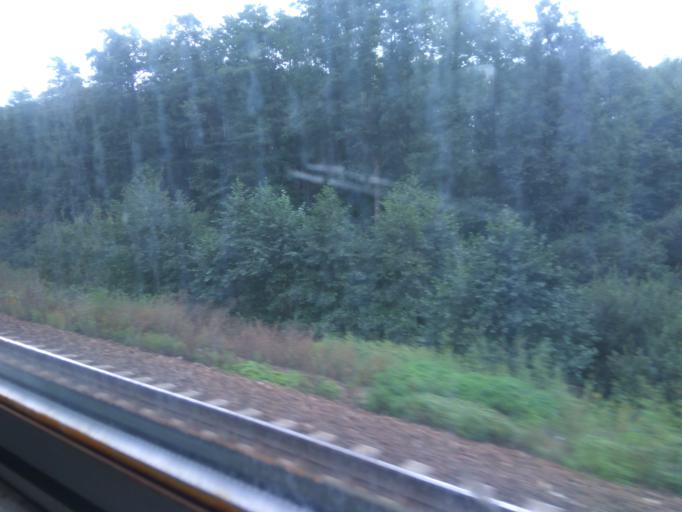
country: RU
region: Moskovskaya
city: Beloozerskiy
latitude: 55.4667
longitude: 38.4394
